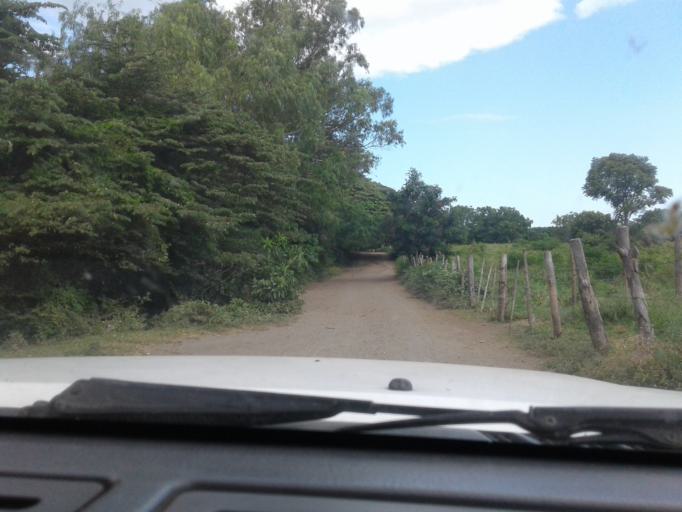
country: NI
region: Rivas
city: Moyogalpa
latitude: 11.5001
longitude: -85.6768
